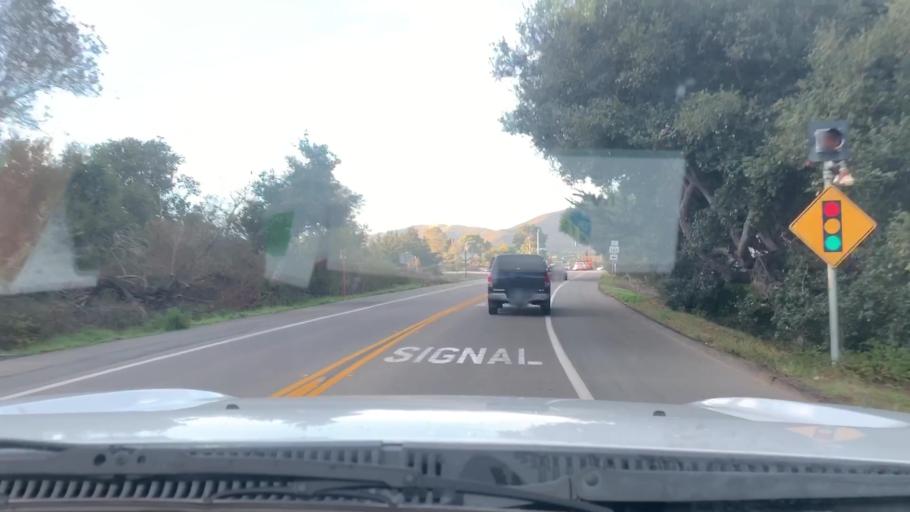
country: US
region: California
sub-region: San Luis Obispo County
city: Los Osos
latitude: 35.3117
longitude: -120.8242
